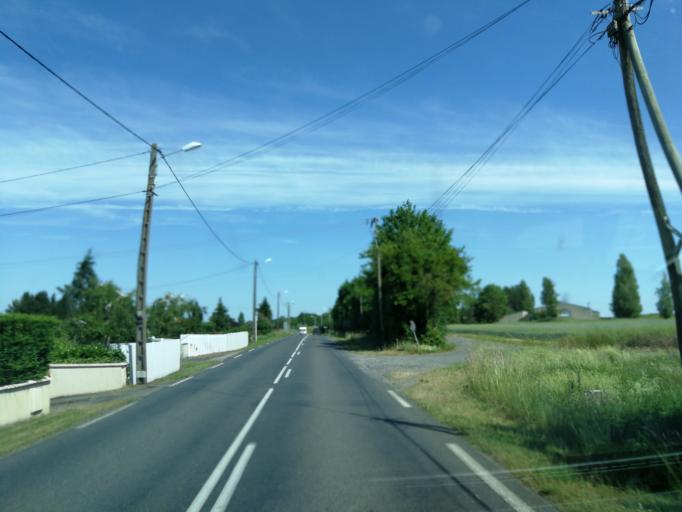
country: FR
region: Poitou-Charentes
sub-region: Departement des Deux-Sevres
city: Saint-Jean-de-Thouars
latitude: 46.9745
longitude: -0.1812
